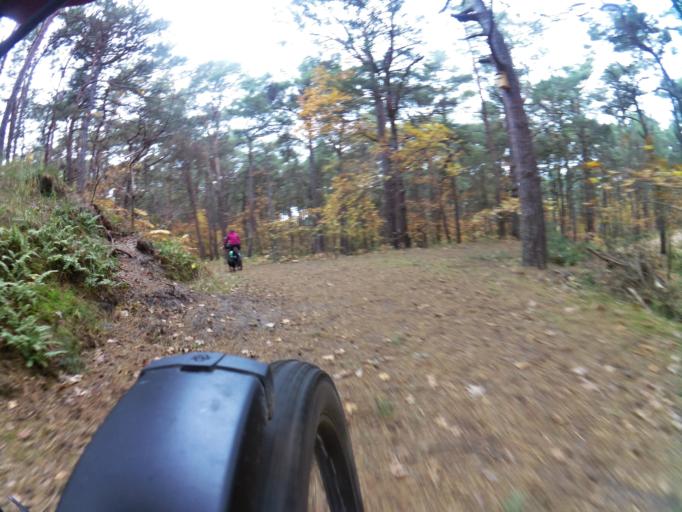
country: PL
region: Pomeranian Voivodeship
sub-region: Powiat pucki
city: Jastarnia
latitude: 54.6939
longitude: 18.6935
